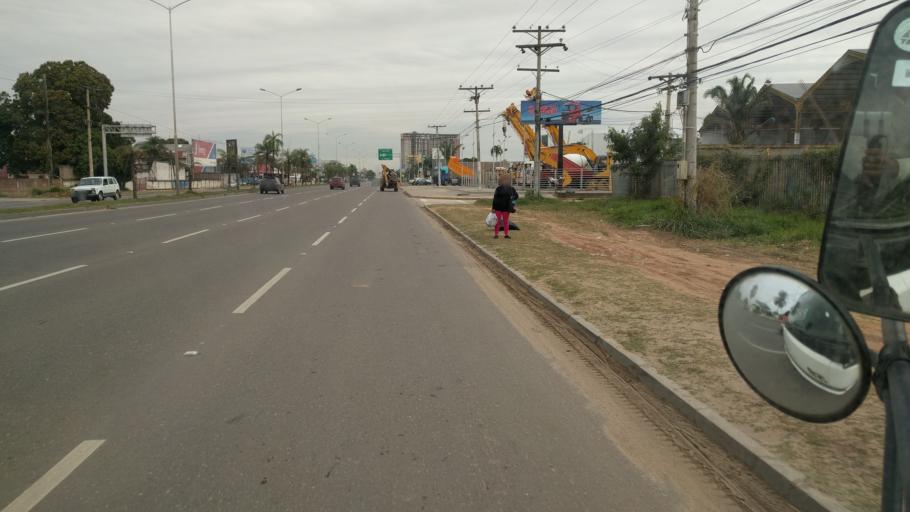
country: BO
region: Santa Cruz
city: Santa Cruz de la Sierra
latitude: -17.7183
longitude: -63.1630
